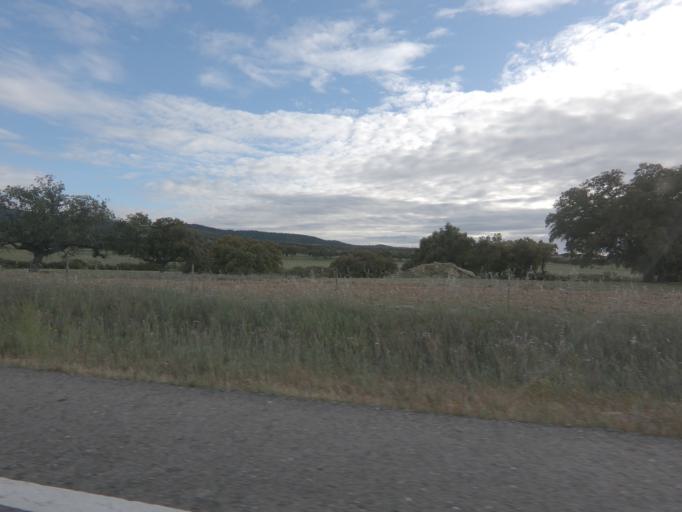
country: ES
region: Extremadura
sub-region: Provincia de Caceres
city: Pedroso de Acim
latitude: 39.8525
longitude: -6.4193
